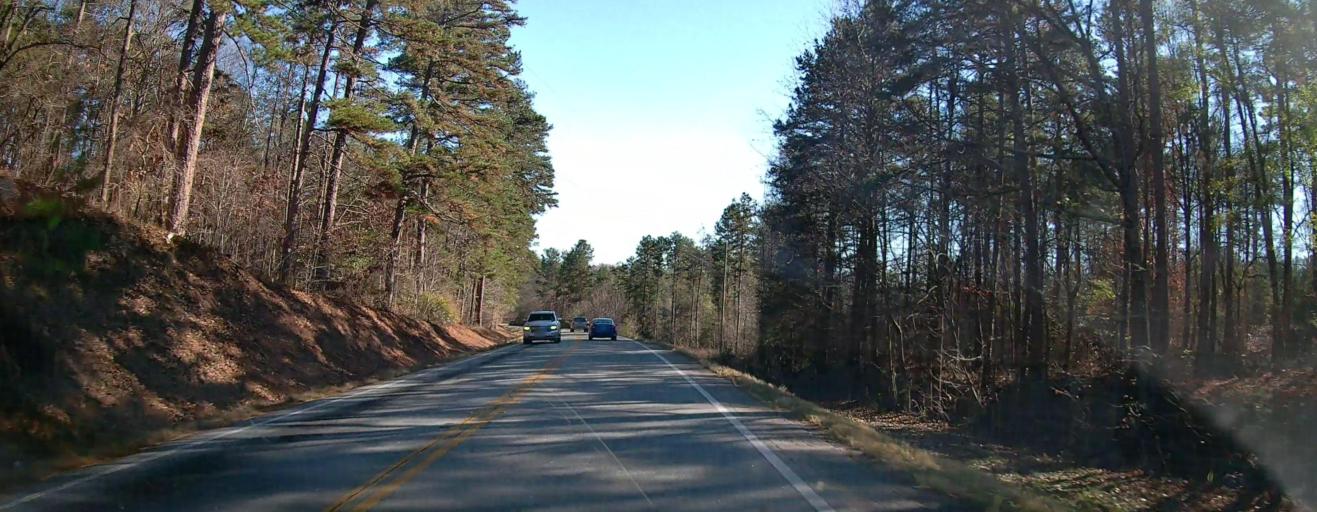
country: US
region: Georgia
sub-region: Hall County
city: Lula
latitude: 34.4232
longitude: -83.7109
